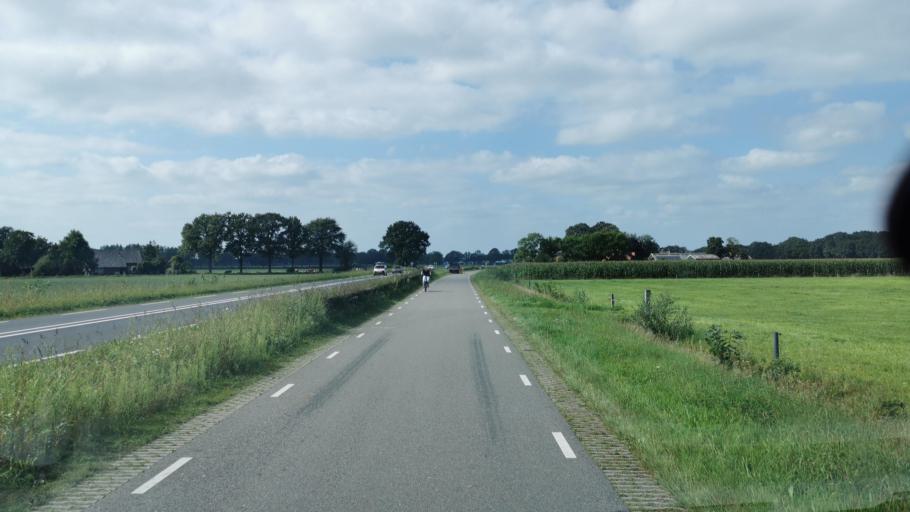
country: NL
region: Overijssel
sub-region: Gemeente Oldenzaal
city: Oldenzaal
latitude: 52.3369
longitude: 6.8753
